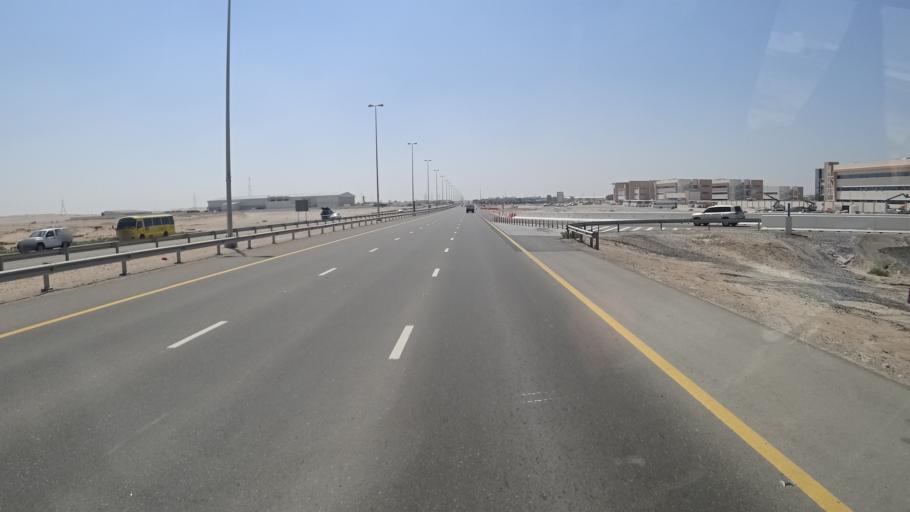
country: AE
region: Abu Dhabi
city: Abu Dhabi
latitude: 24.3147
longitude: 54.6778
